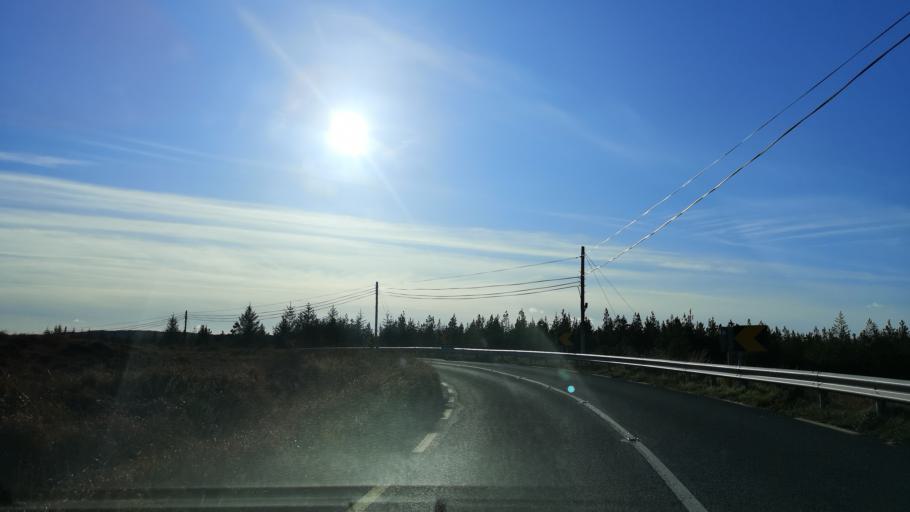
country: IE
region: Connaught
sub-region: County Galway
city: Clifden
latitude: 53.5279
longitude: -10.0477
